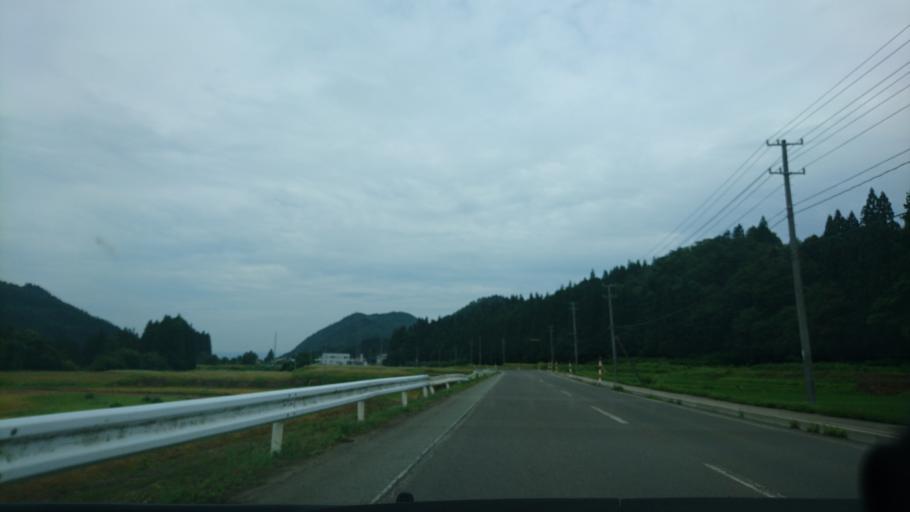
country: JP
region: Akita
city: Yuzawa
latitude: 39.1968
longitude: 140.6126
